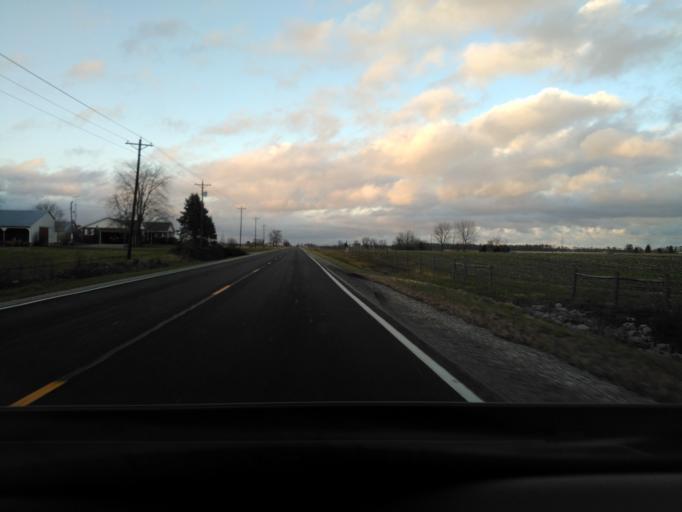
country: US
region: Illinois
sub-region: Effingham County
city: Altamont
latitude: 38.9939
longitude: -88.7487
